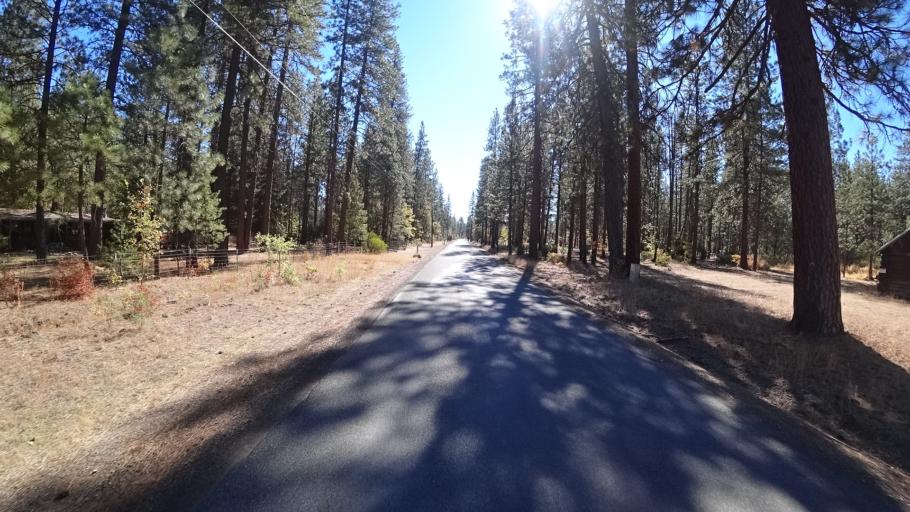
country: US
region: California
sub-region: Siskiyou County
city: Yreka
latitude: 41.6035
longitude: -122.9759
